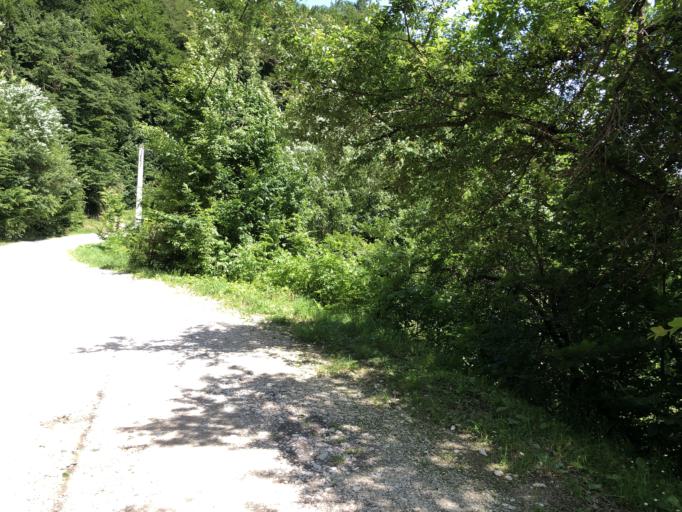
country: RO
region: Brasov
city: Brasov
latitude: 45.6264
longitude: 25.5954
